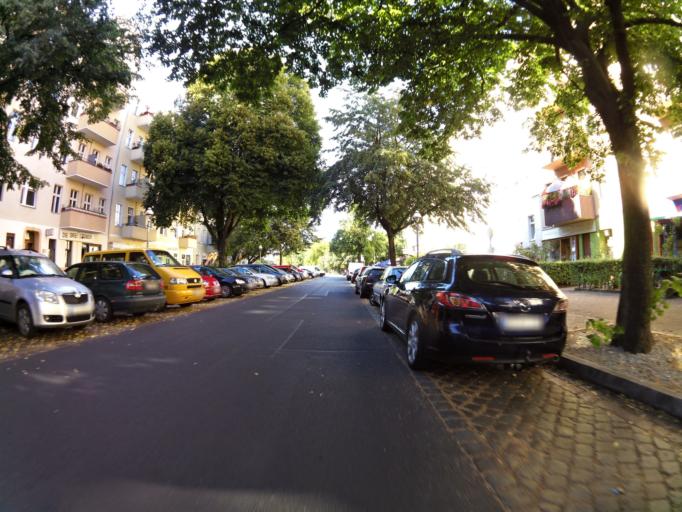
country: DE
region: Berlin
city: Wedding Bezirk
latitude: 52.5425
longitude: 13.3568
